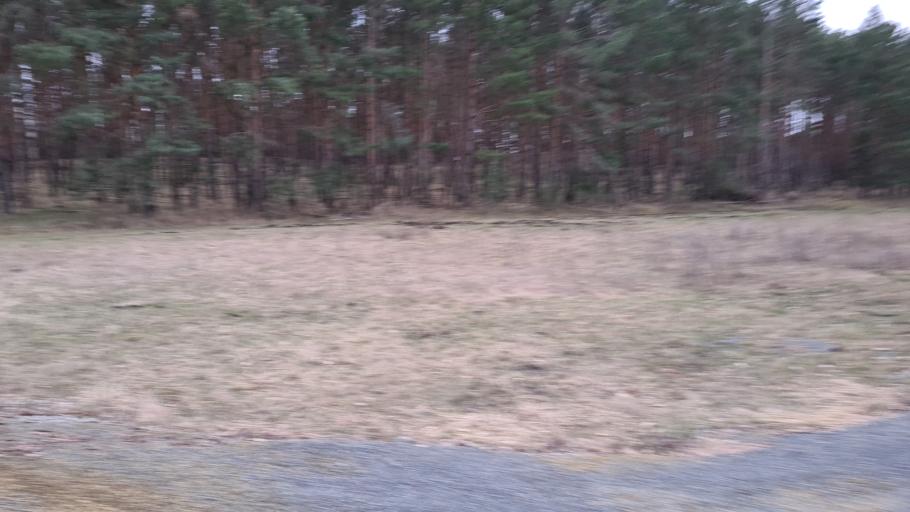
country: DE
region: Brandenburg
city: Schonborn
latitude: 51.5866
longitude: 13.4635
